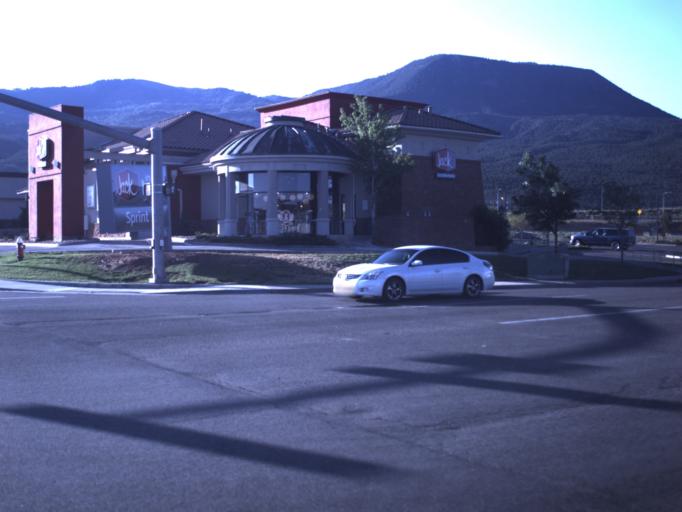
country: US
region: Utah
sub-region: Iron County
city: Cedar City
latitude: 37.6550
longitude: -113.0852
